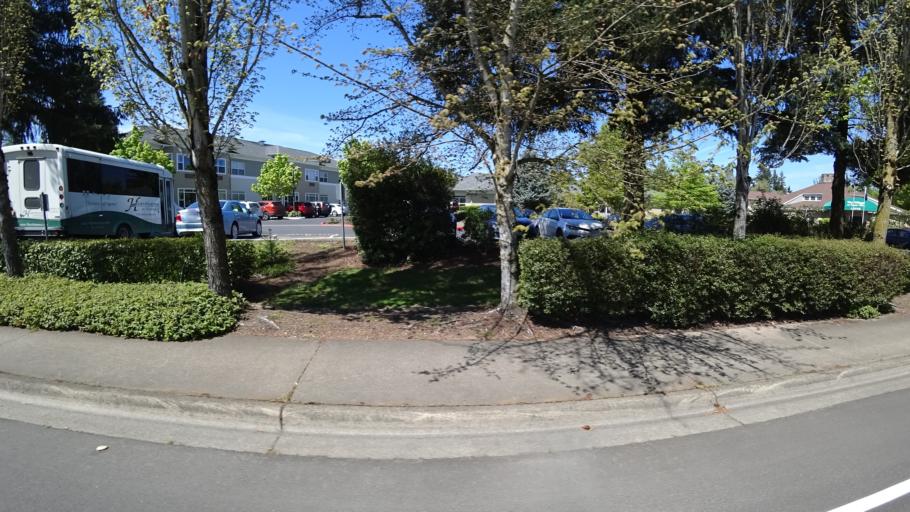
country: US
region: Oregon
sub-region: Washington County
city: King City
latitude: 45.4405
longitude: -122.8193
